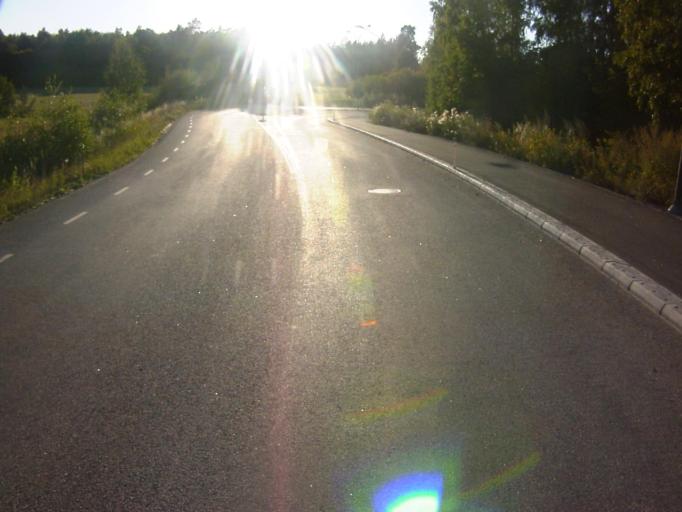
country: SE
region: Soedermanland
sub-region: Eskilstuna Kommun
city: Hallbybrunn
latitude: 59.3997
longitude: 16.4116
